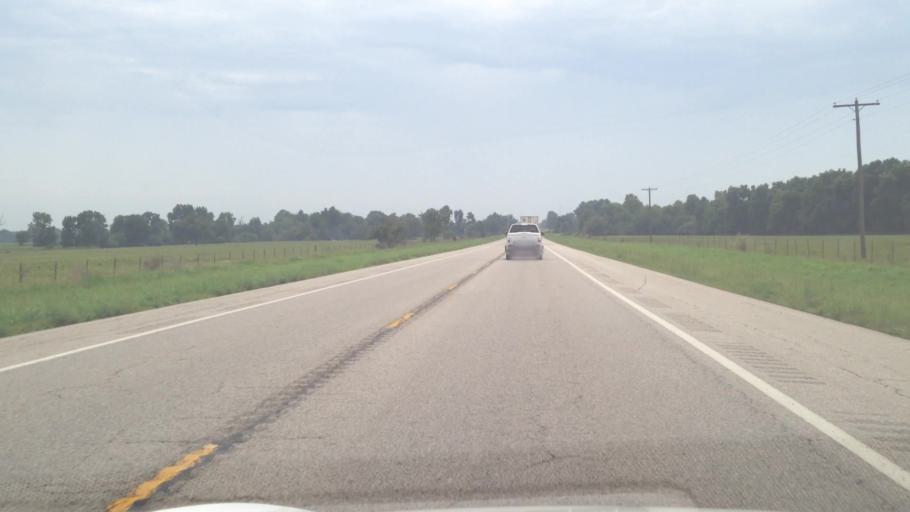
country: US
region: Missouri
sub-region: Jasper County
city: Carl Junction
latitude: 37.2070
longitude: -94.7048
